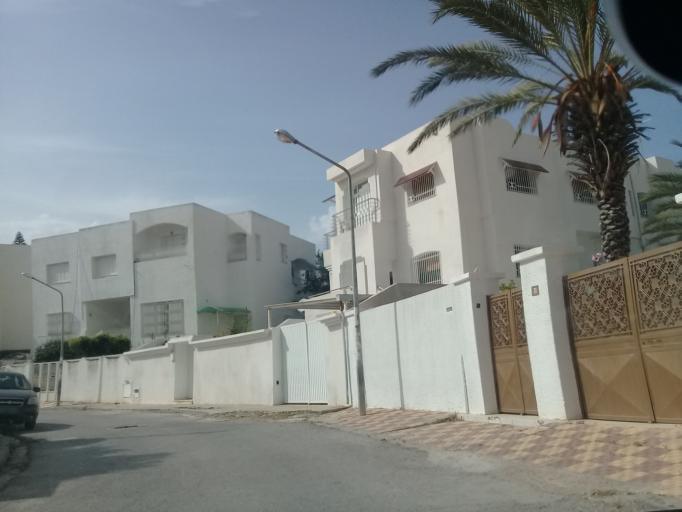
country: TN
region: Tunis
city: Tunis
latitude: 36.8513
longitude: 10.1613
